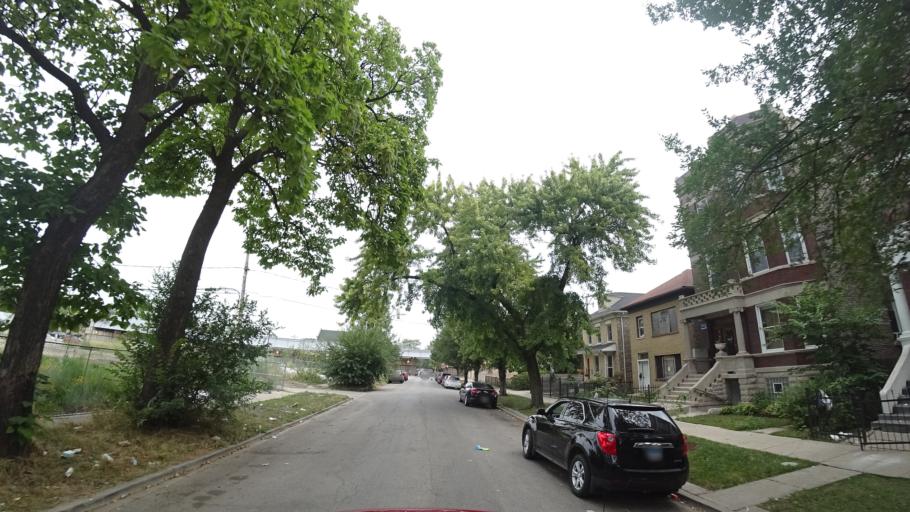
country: US
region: Illinois
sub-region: Cook County
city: Cicero
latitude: 41.8530
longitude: -87.7163
